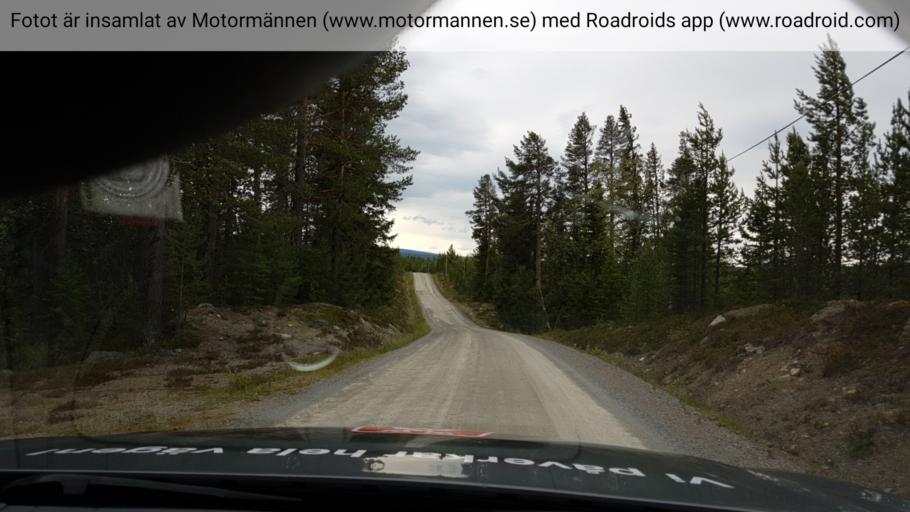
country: SE
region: Jaemtland
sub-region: Are Kommun
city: Jarpen
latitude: 62.8018
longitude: 13.8019
